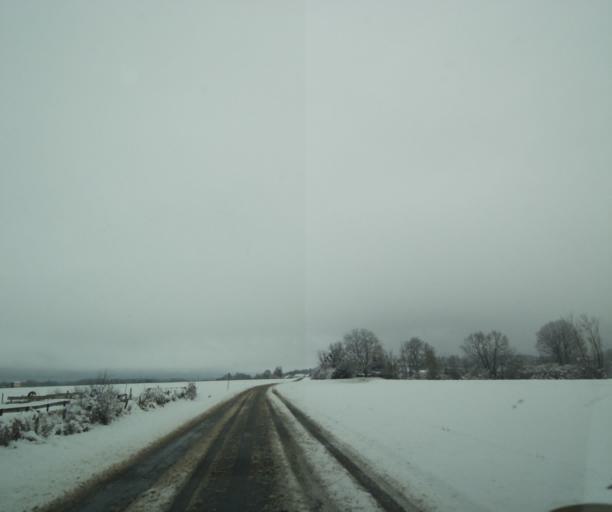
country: FR
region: Champagne-Ardenne
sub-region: Departement de la Haute-Marne
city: Wassy
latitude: 48.5666
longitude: 4.8929
